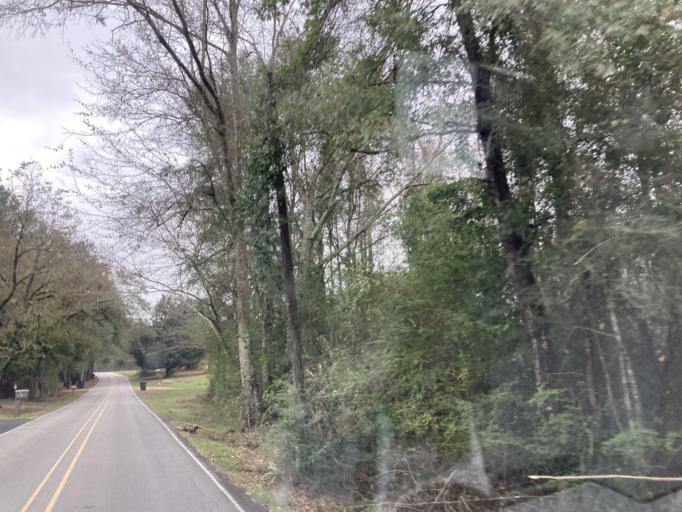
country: US
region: Mississippi
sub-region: Lamar County
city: Purvis
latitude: 31.1797
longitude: -89.4199
